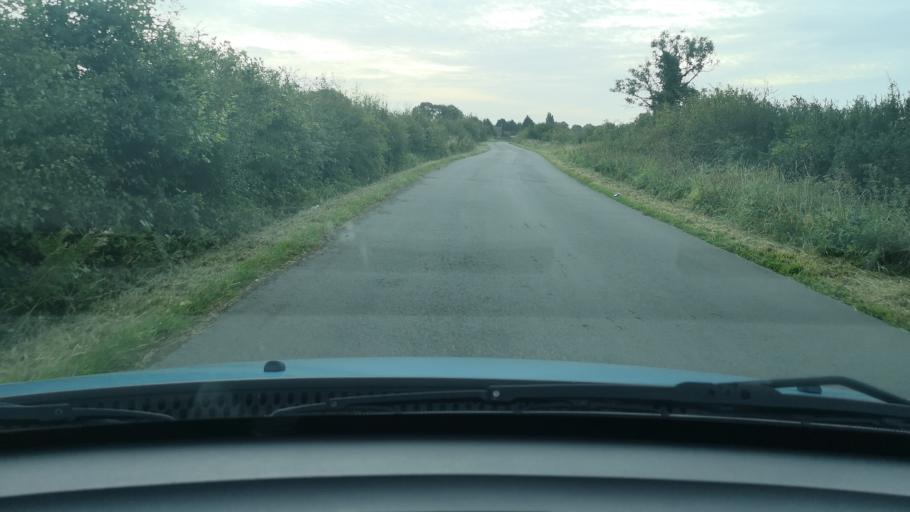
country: GB
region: England
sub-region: Doncaster
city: Stainforth
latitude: 53.6297
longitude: -1.0263
